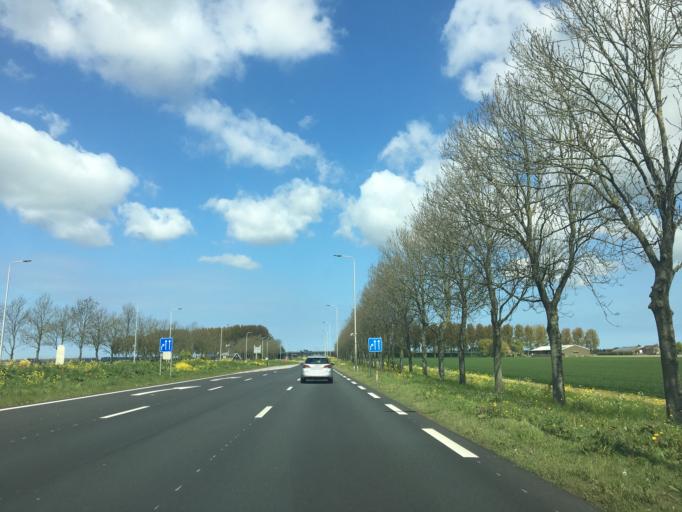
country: NL
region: South Holland
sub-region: Gemeente Kaag en Braassem
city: Leimuiden
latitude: 52.2415
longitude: 4.6507
